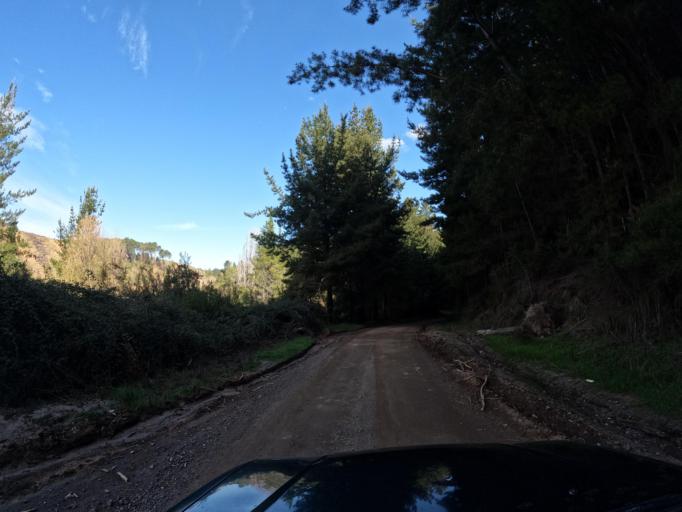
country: CL
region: Biobio
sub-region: Provincia de Concepcion
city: Chiguayante
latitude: -37.0758
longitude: -72.8372
